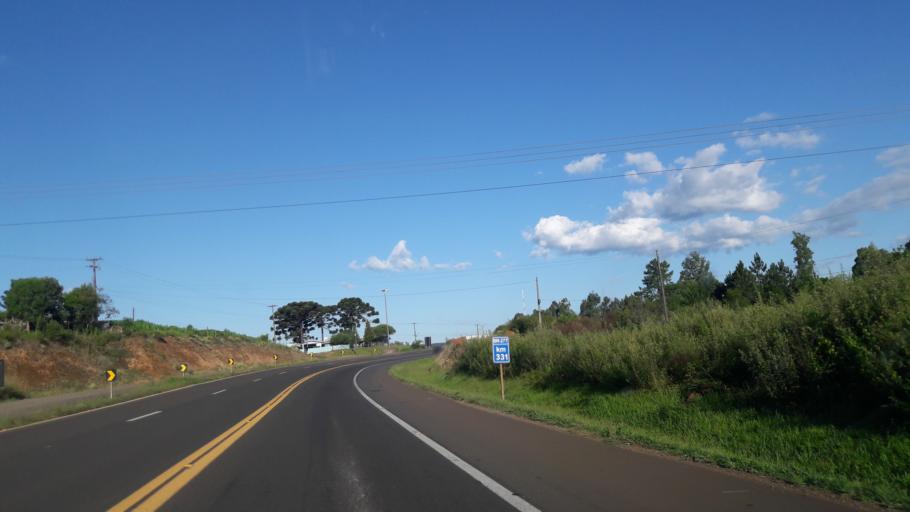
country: BR
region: Parana
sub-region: Guarapuava
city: Guarapuava
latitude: -25.3526
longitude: -51.3681
